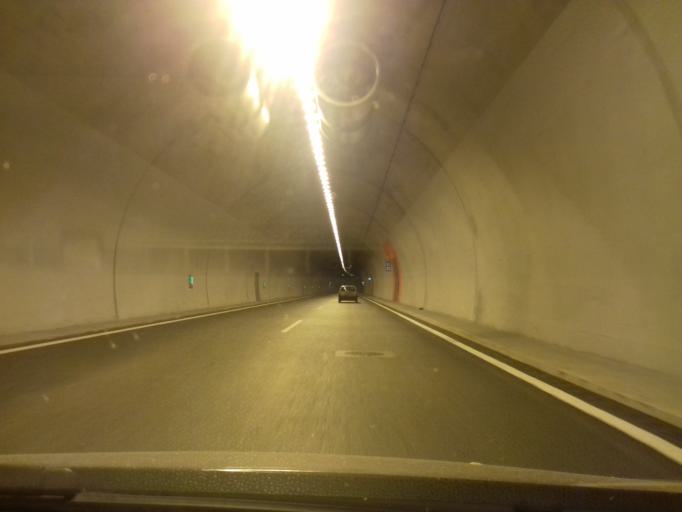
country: GR
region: West Greece
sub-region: Nomos Achaias
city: Akrata
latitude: 38.1668
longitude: 22.2773
